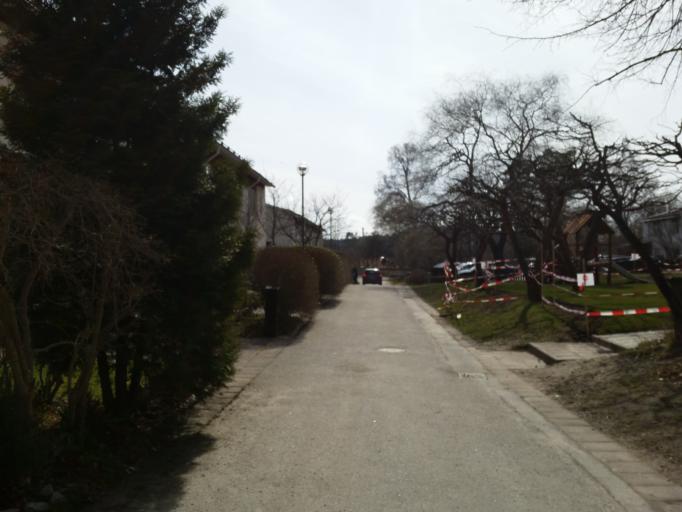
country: SE
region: Stockholm
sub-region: Norrtalje Kommun
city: Bergshamra
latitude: 59.3785
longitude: 18.0315
